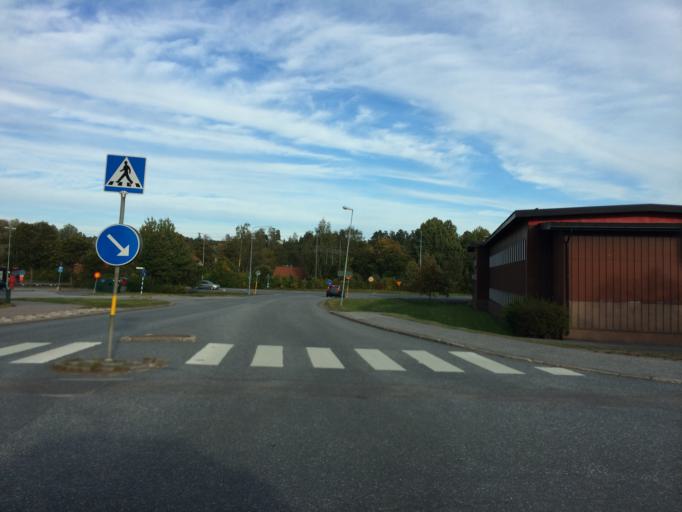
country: SE
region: Stockholm
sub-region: Sollentuna Kommun
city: Sollentuna
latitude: 59.4569
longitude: 17.9223
